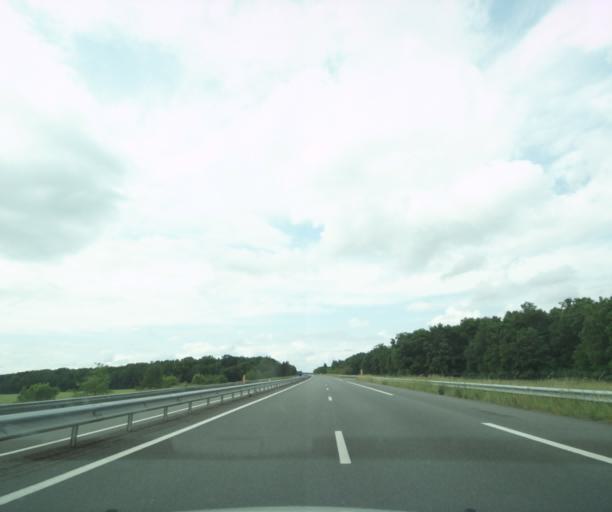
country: FR
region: Centre
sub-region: Departement du Cher
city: Levet
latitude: 46.8701
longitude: 2.4261
